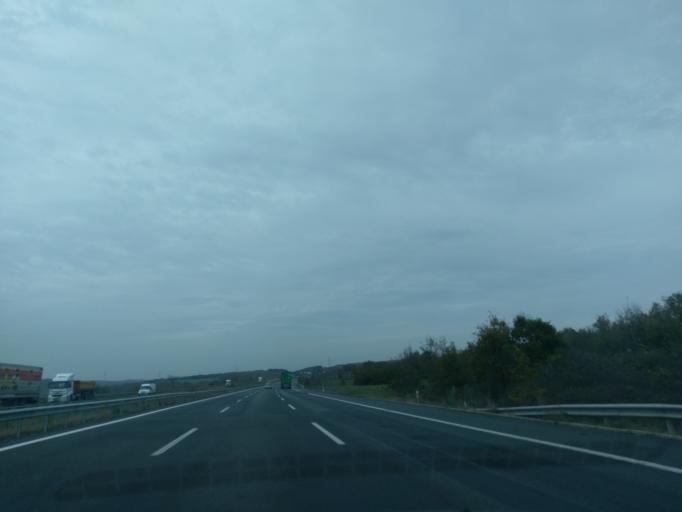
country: TR
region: Istanbul
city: Canta
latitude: 41.1723
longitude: 28.1193
